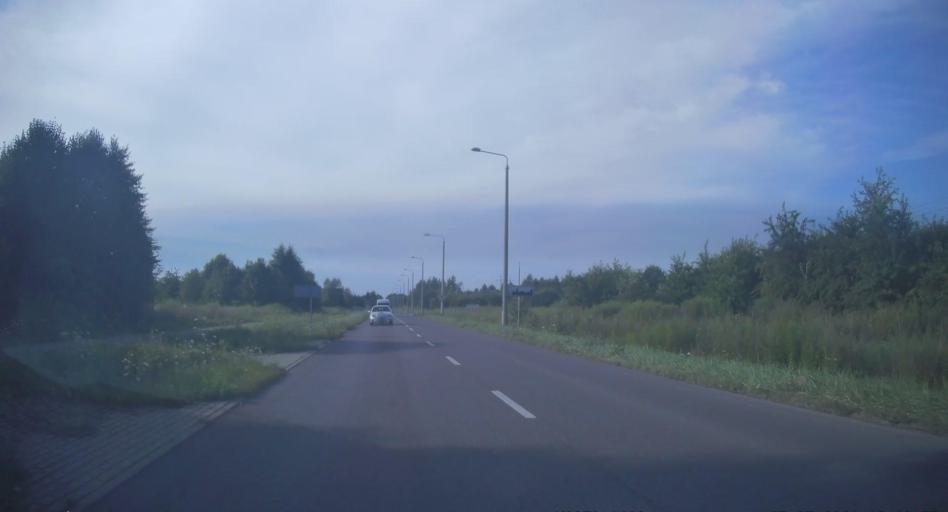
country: PL
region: Swietokrzyskie
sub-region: Powiat konecki
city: Konskie
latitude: 51.2125
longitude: 20.3940
